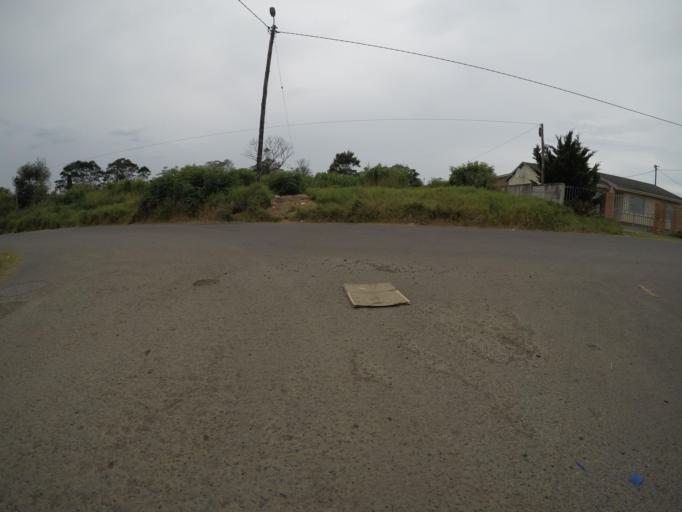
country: ZA
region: Eastern Cape
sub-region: Buffalo City Metropolitan Municipality
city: East London
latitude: -32.9979
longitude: 27.8481
